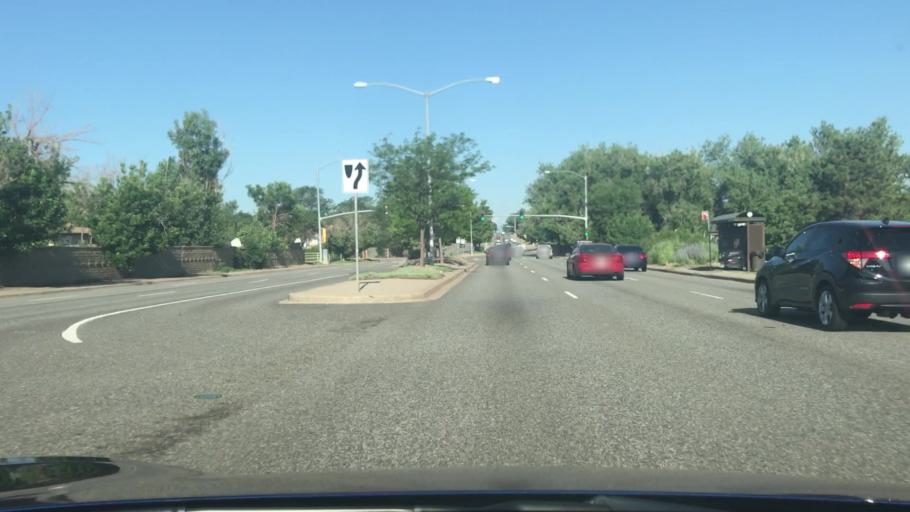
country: US
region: Colorado
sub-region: Arapahoe County
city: Dove Valley
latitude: 39.6531
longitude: -104.7964
